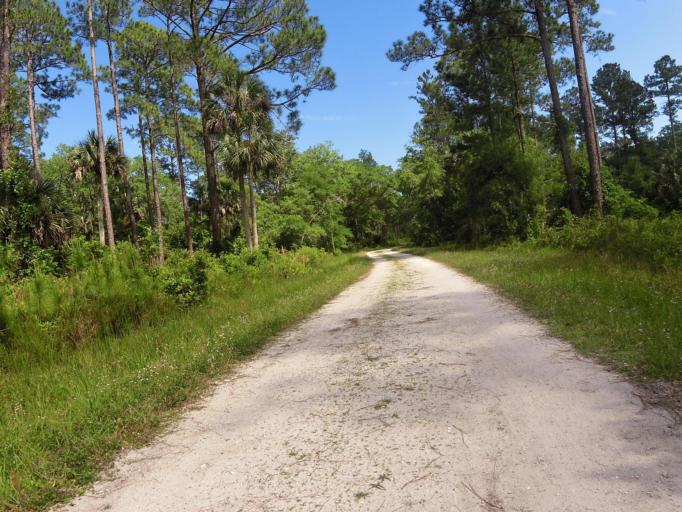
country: US
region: Florida
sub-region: Saint Johns County
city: Palm Valley
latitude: 30.1409
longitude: -81.3739
